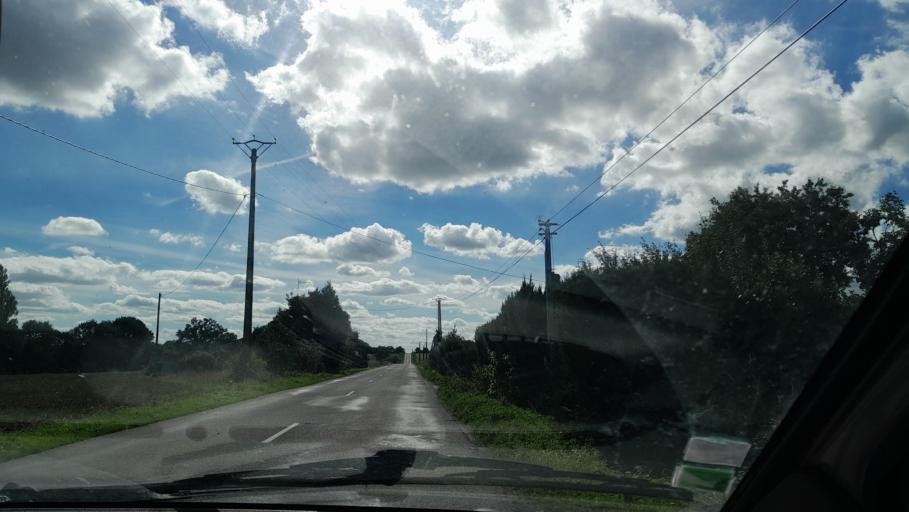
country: FR
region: Pays de la Loire
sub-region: Departement de la Mayenne
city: Ballots
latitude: 47.9598
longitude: -1.0543
